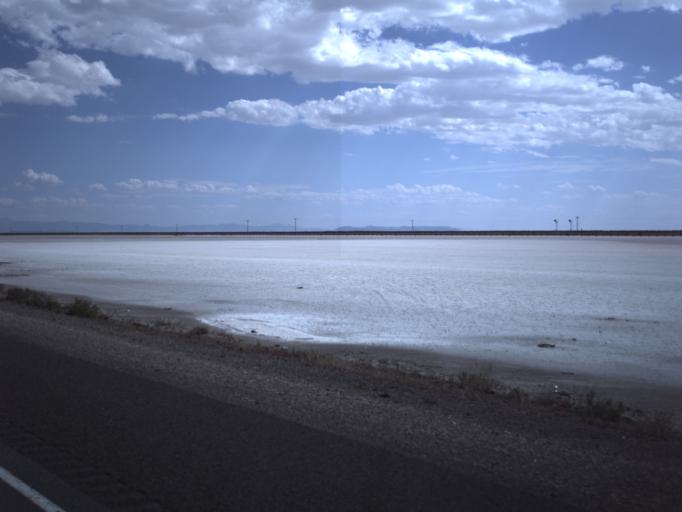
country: US
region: Utah
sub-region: Tooele County
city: Wendover
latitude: 40.7351
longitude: -113.6869
